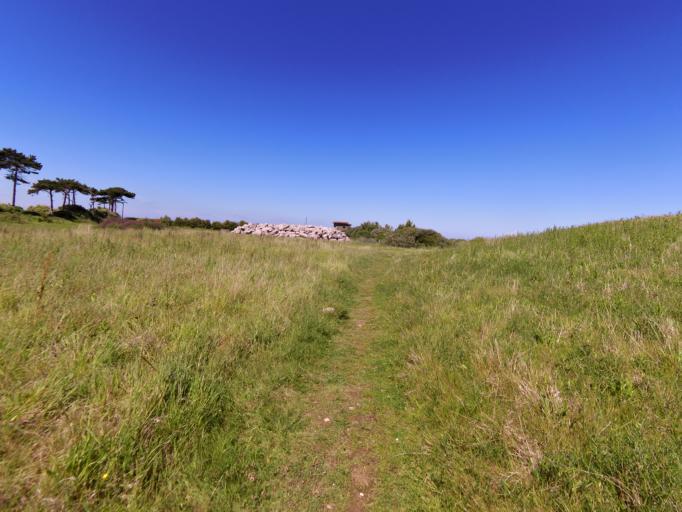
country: GB
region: England
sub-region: Suffolk
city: Felixstowe
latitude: 52.0078
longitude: 1.4320
